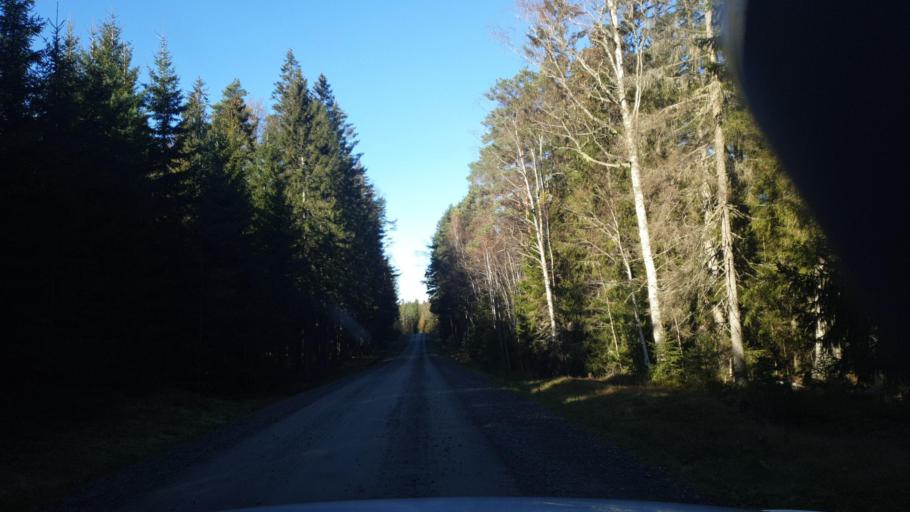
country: SE
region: Vaermland
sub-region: Karlstads Kommun
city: Valberg
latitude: 59.4507
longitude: 13.1037
